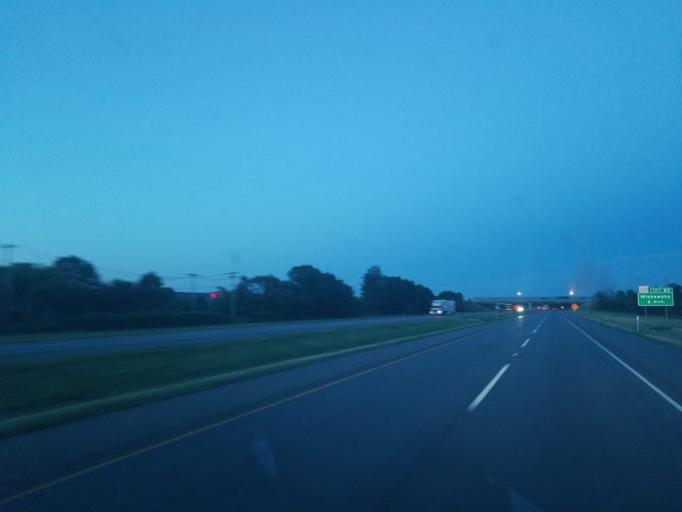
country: US
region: Indiana
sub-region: Saint Joseph County
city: Georgetown
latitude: 41.7162
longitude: -86.1826
